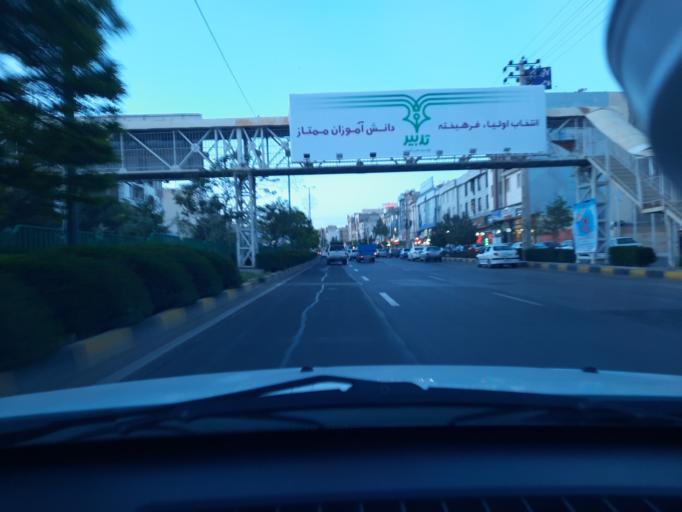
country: IR
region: Qazvin
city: Qazvin
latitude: 36.3079
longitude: 50.0125
